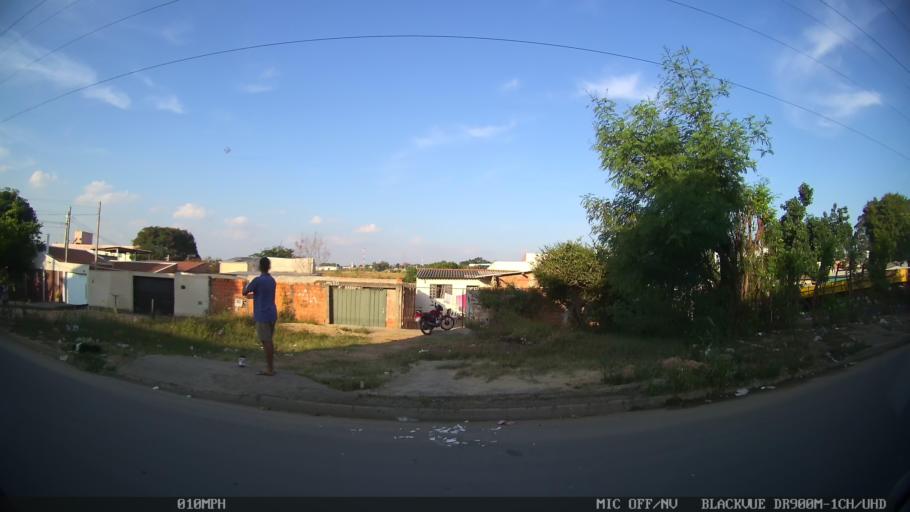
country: BR
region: Sao Paulo
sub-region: Campinas
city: Campinas
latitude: -22.9879
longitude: -47.1167
